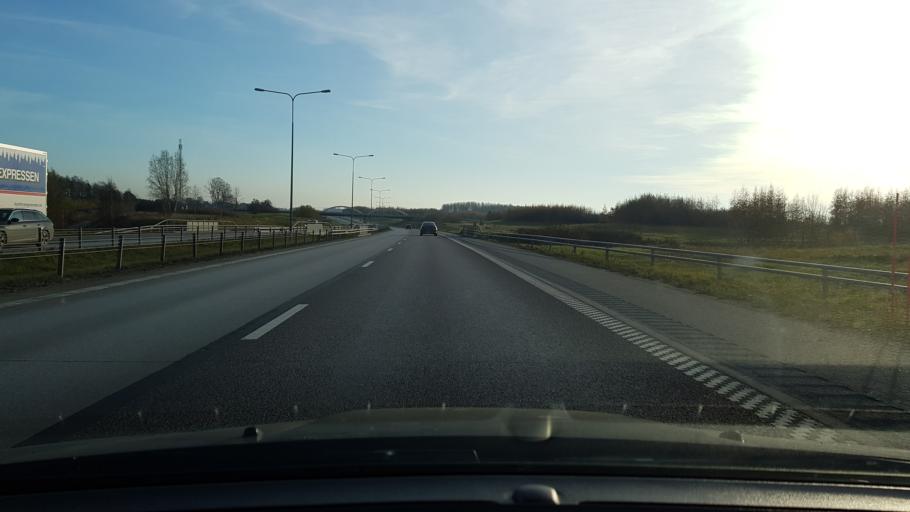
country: SE
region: Uppsala
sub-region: Uppsala Kommun
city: Saevja
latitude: 59.8706
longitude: 17.7041
